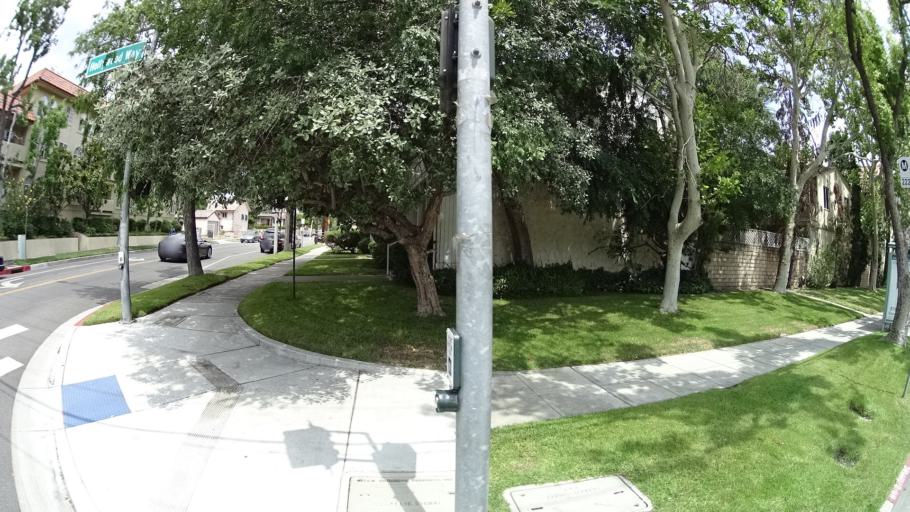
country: US
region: California
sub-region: Los Angeles County
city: Universal City
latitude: 34.1575
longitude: -118.3419
